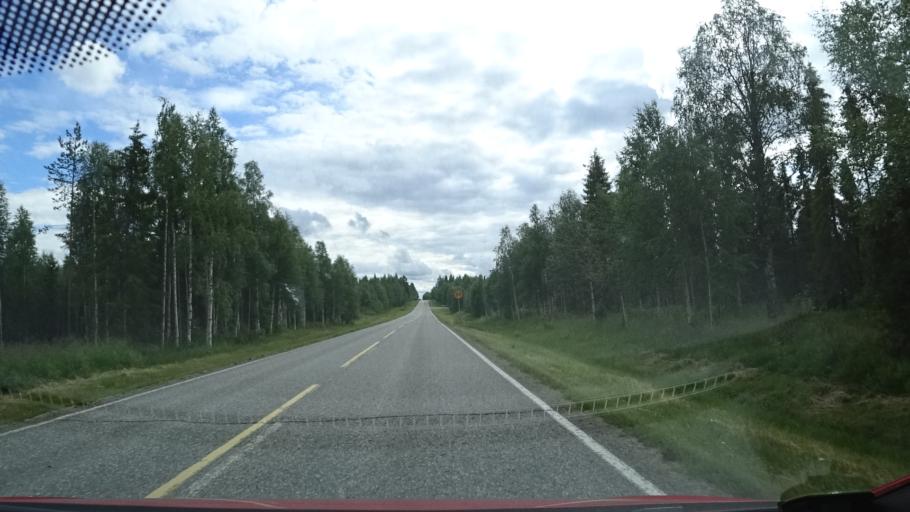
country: FI
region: Lapland
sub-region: Tunturi-Lappi
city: Kittilae
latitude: 67.4767
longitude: 24.9340
